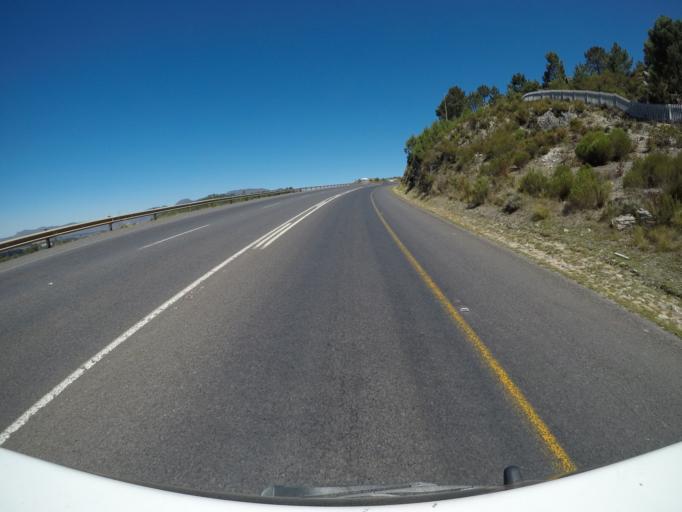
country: ZA
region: Western Cape
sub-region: Overberg District Municipality
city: Grabouw
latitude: -34.1667
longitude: 19.0006
